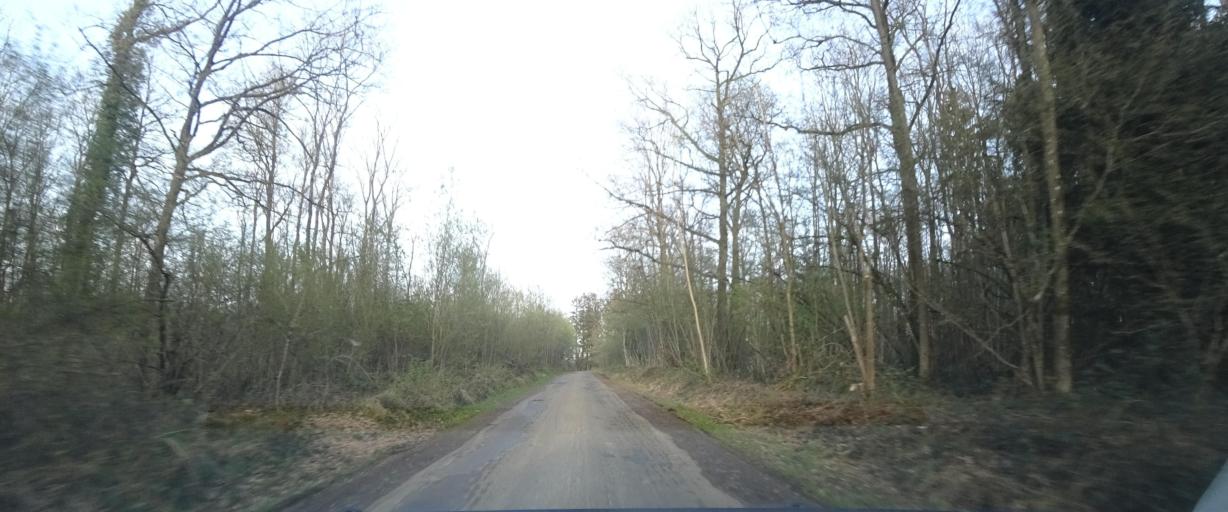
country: BE
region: Wallonia
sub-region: Province de Namur
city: Hamois
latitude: 50.3100
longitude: 5.1739
